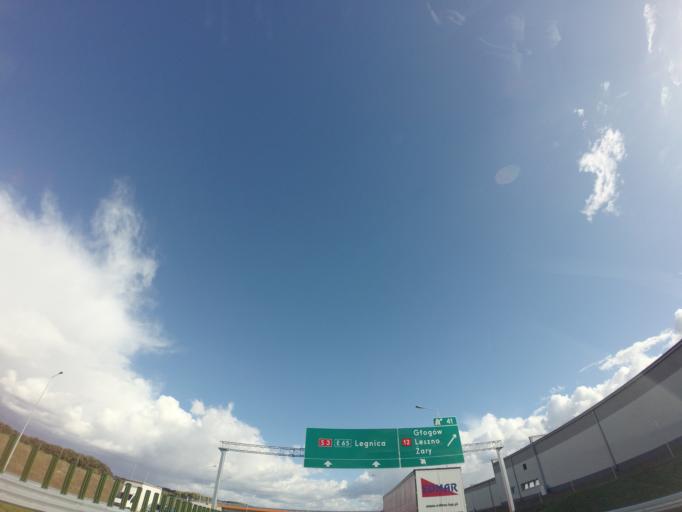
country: PL
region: Lower Silesian Voivodeship
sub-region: Powiat polkowicki
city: Radwanice
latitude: 51.6010
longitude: 15.9609
